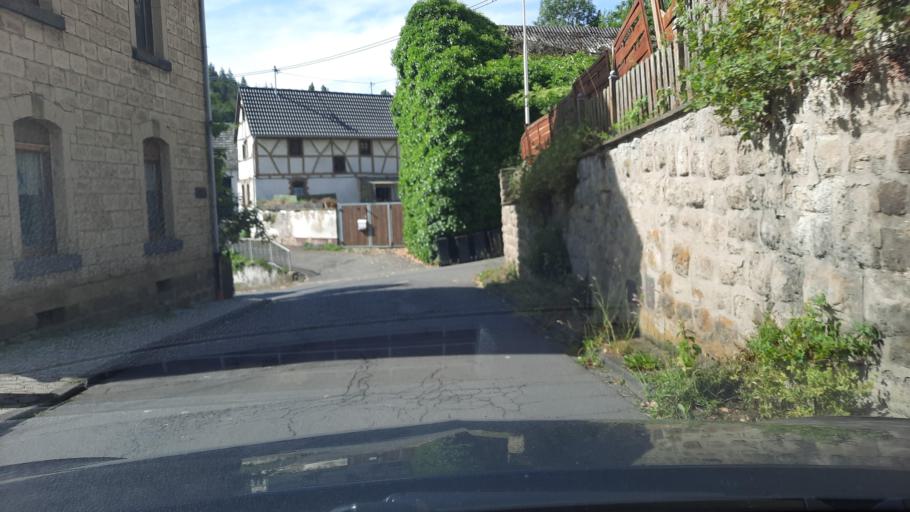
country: DE
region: Rheinland-Pfalz
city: Brenk
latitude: 50.4318
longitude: 7.1721
